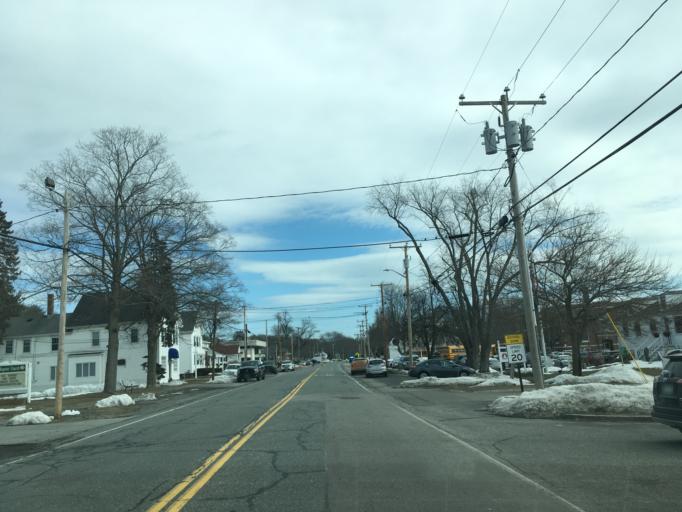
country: US
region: New Hampshire
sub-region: Rockingham County
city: Hampton
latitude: 42.9378
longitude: -70.8369
